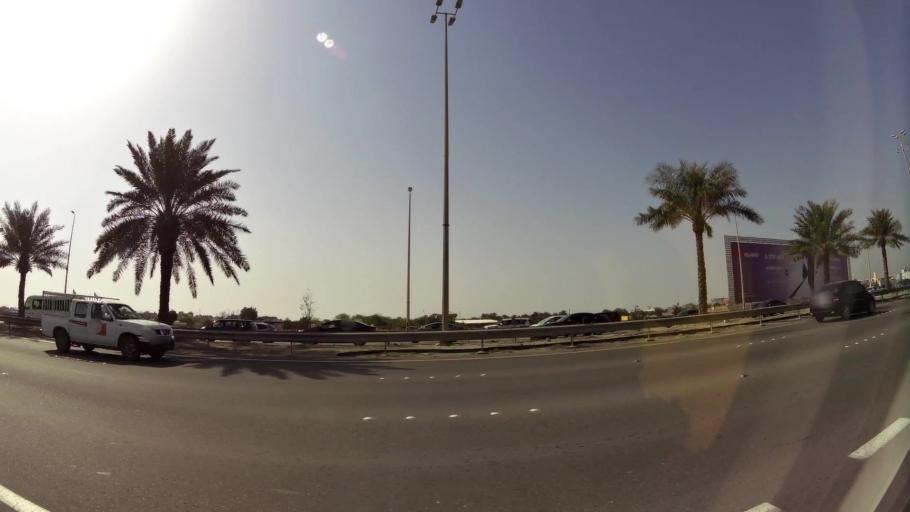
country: BH
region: Manama
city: Jidd Hafs
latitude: 26.2120
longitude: 50.5191
